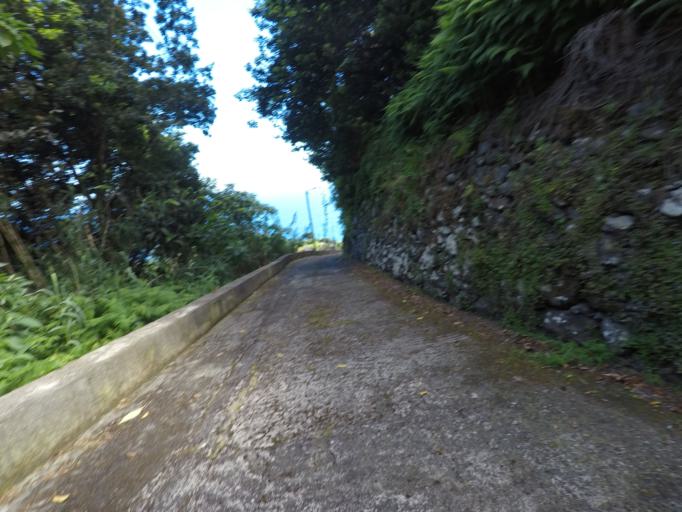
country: PT
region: Madeira
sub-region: Santana
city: Santana
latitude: 32.8231
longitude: -16.9496
